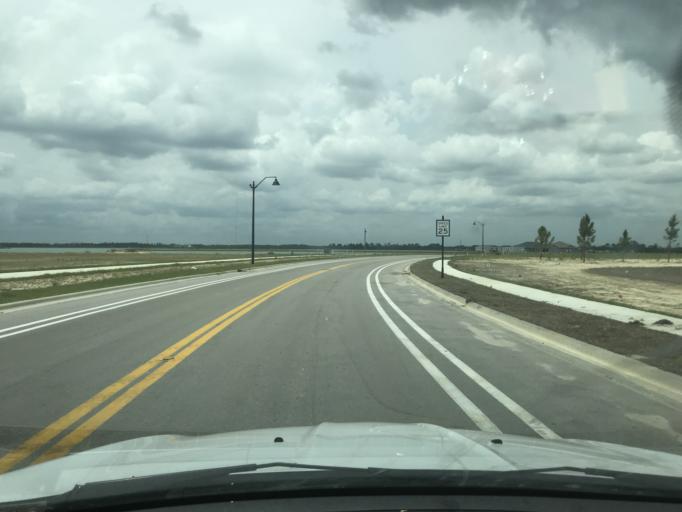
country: US
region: Florida
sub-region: Lee County
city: Olga
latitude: 26.7852
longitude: -81.7383
